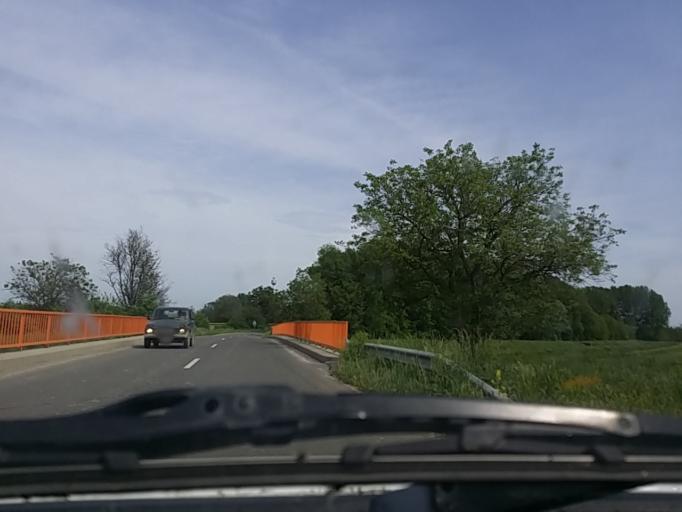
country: HU
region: Baranya
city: Vajszlo
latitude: 45.8448
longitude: 18.0297
